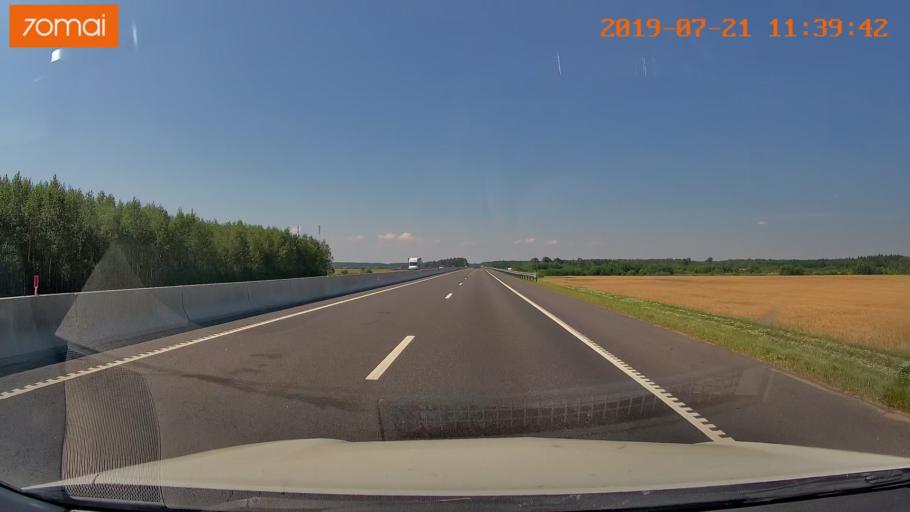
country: BY
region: Grodnenskaya
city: Lyubcha
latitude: 53.9584
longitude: 26.1930
